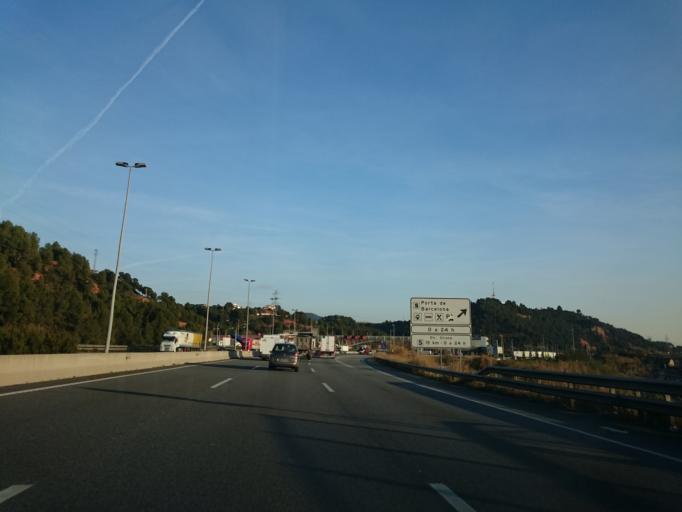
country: ES
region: Catalonia
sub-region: Provincia de Barcelona
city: Castellbisbal
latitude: 41.4690
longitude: 1.9742
